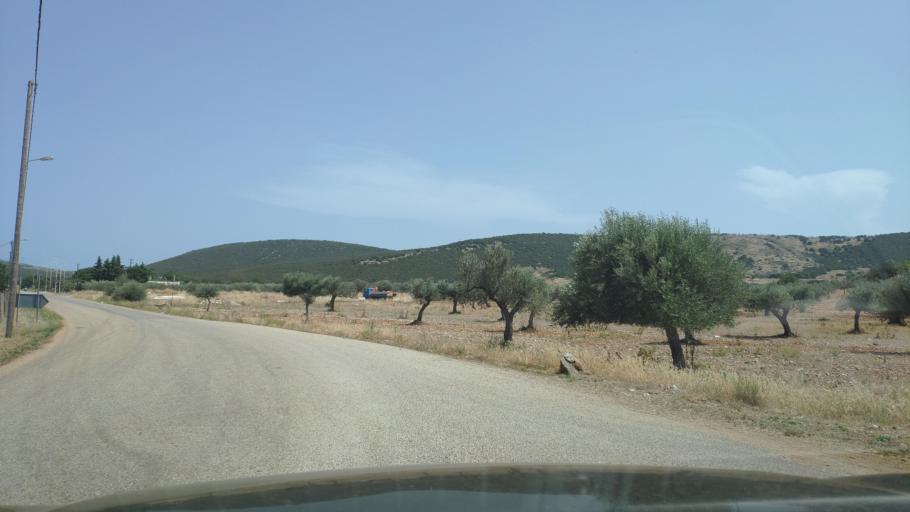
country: GR
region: Peloponnese
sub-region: Nomos Argolidos
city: Didyma
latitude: 37.4560
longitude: 23.1687
